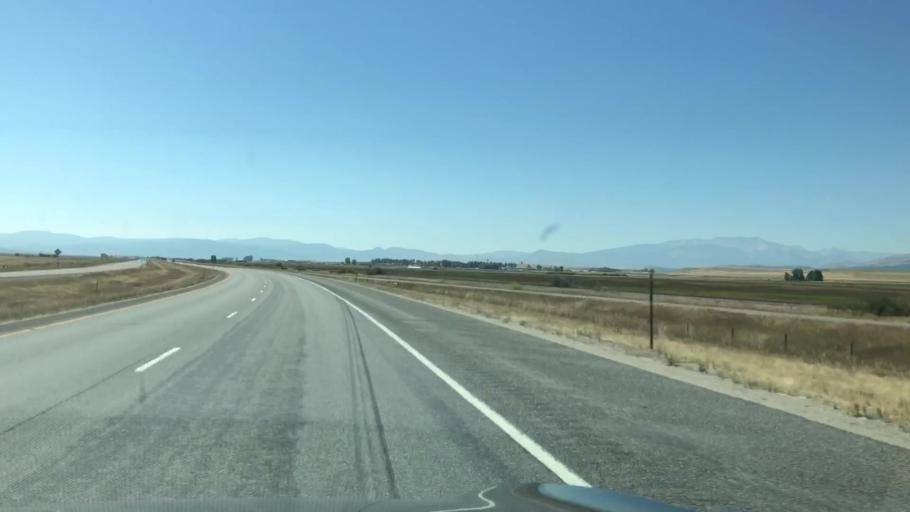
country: US
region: Montana
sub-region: Deer Lodge County
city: Warm Springs
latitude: 46.2589
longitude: -112.7580
